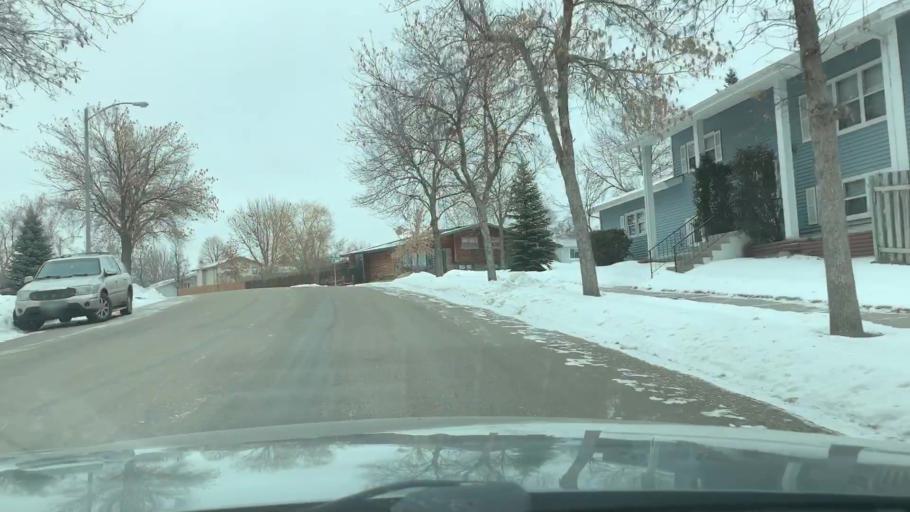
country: US
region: North Dakota
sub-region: Burleigh County
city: Bismarck
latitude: 46.8250
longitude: -100.8070
